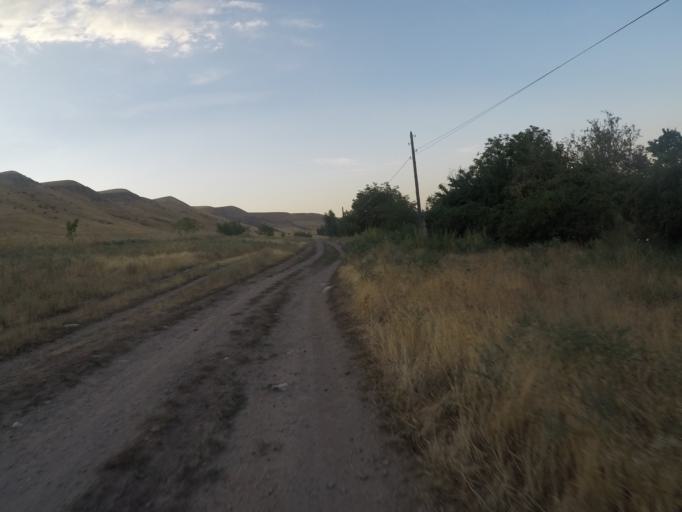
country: KG
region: Chuy
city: Bishkek
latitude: 42.7679
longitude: 74.6386
